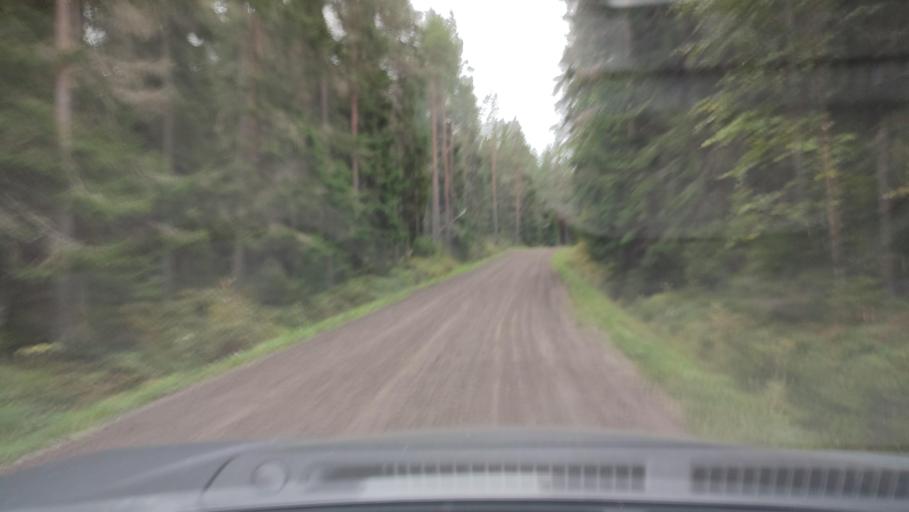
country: FI
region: Southern Ostrobothnia
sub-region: Suupohja
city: Karijoki
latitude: 62.2315
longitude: 21.5733
